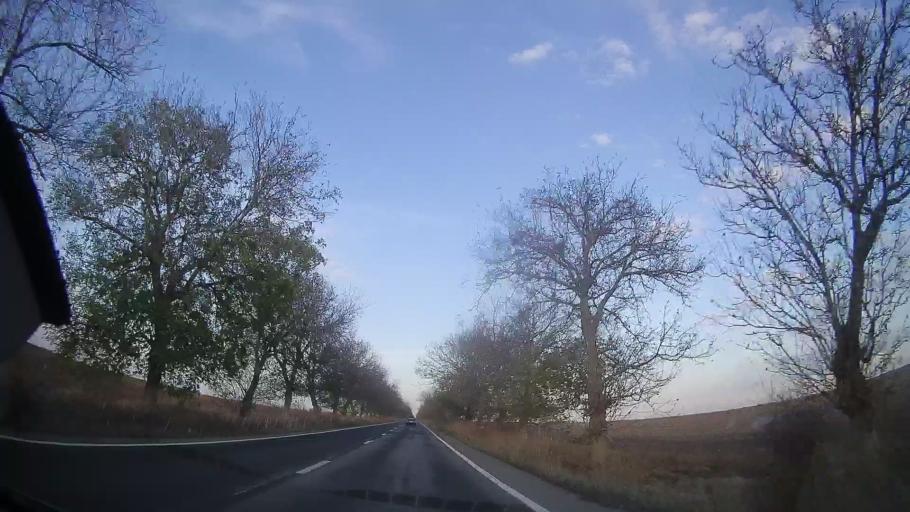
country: RO
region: Constanta
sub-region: Comuna Chirnogeni
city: Chirnogeni
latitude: 43.8660
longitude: 28.2664
